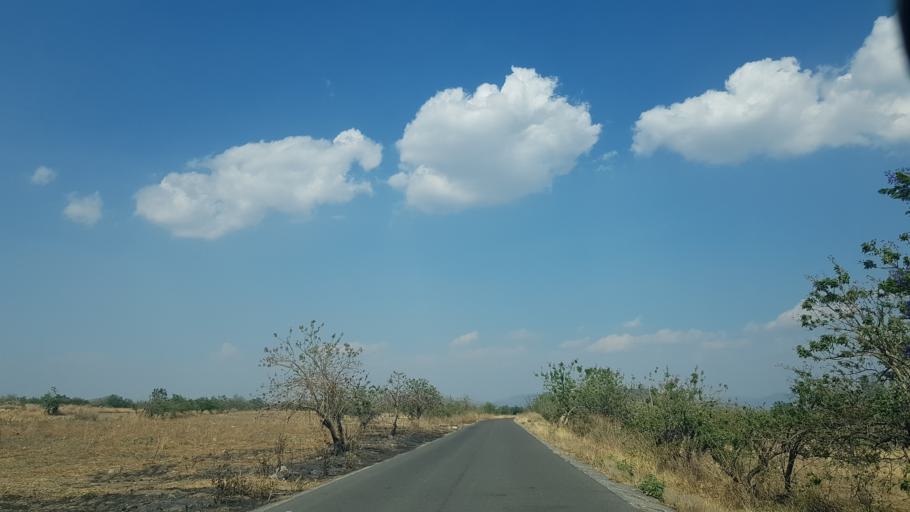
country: MX
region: Puebla
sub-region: Atlixco
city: Colonia Agricola de Ocotepec (Colonia San Jose)
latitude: 18.9226
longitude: -98.5099
